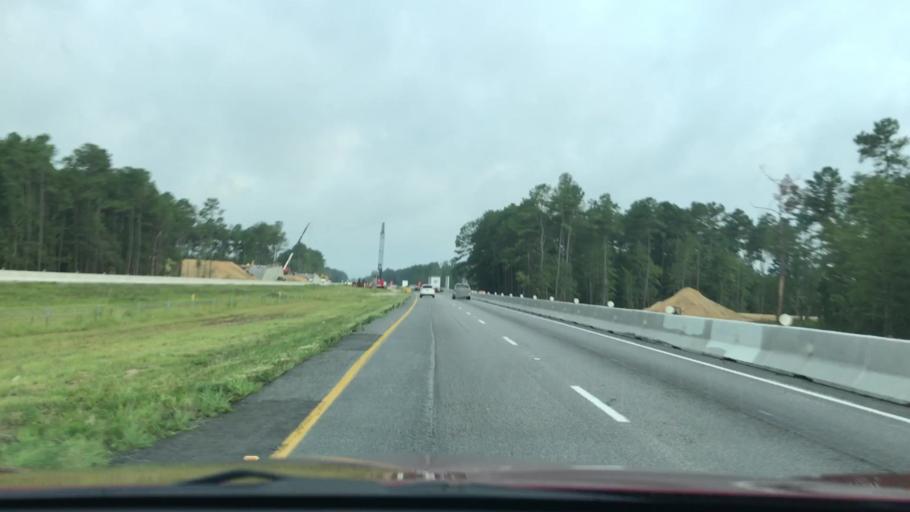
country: US
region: South Carolina
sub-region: Dorchester County
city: Ridgeville
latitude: 33.1192
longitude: -80.2735
